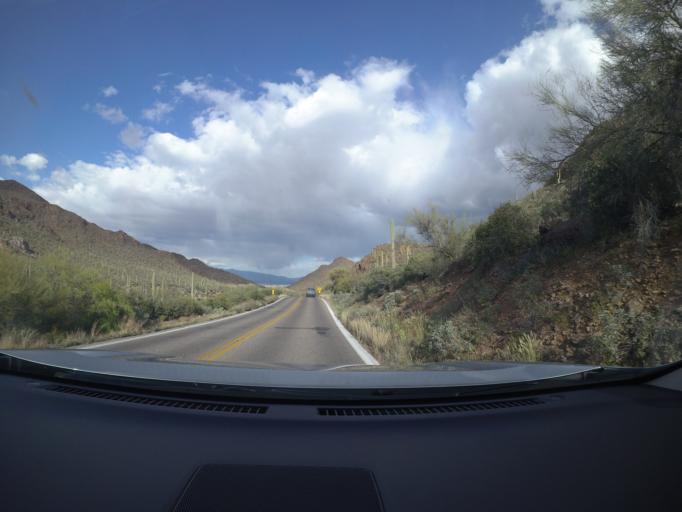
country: US
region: Arizona
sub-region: Pima County
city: Tucson Estates
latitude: 32.2235
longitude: -111.0970
